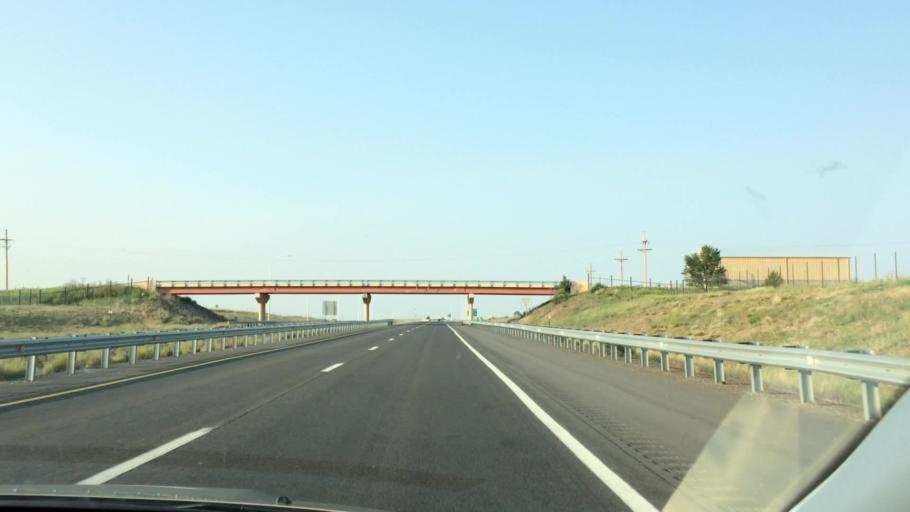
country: US
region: New Mexico
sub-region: Colfax County
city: Raton
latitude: 36.8716
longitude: -104.4366
